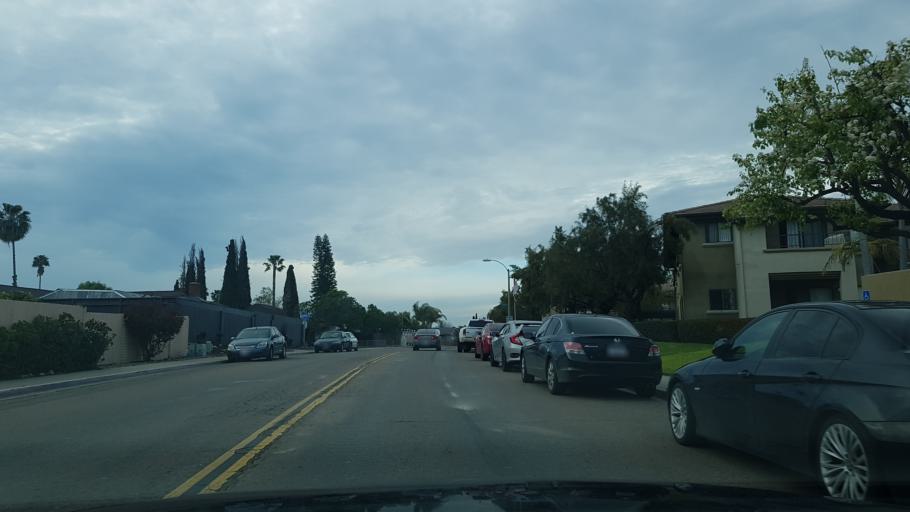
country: US
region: California
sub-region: San Diego County
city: Fairbanks Ranch
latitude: 32.9094
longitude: -117.1477
